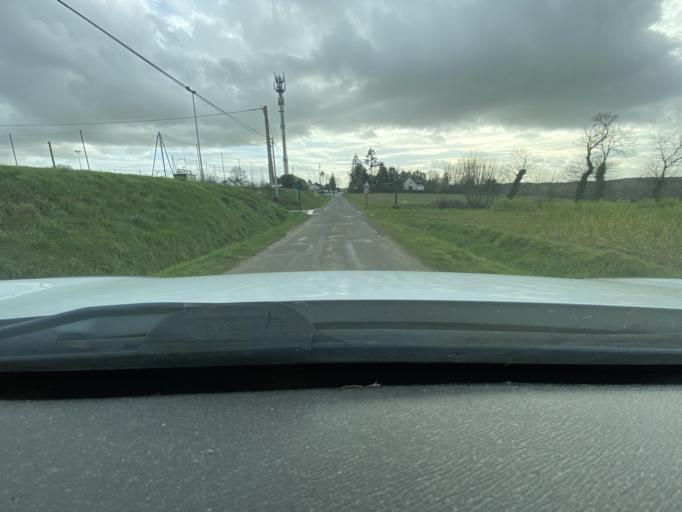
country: FR
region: Brittany
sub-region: Departement d'Ille-et-Vilaine
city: Melesse
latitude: 48.2205
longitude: -1.7081
